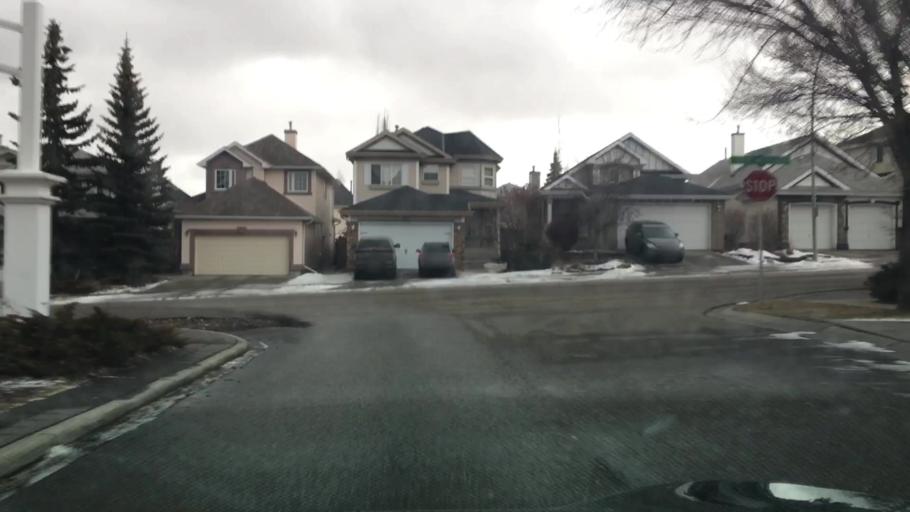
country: CA
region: Alberta
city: Calgary
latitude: 51.1470
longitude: -114.1189
